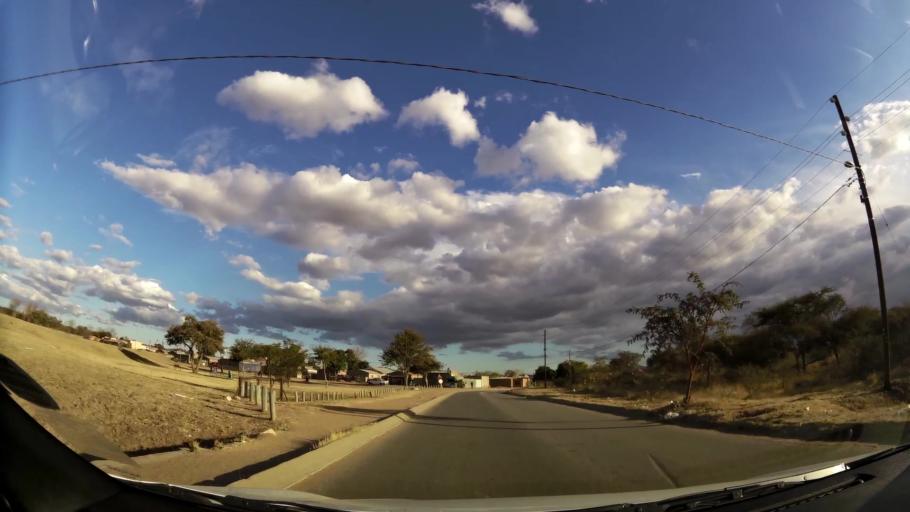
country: ZA
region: Limpopo
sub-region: Capricorn District Municipality
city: Polokwane
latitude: -23.9177
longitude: 29.4220
